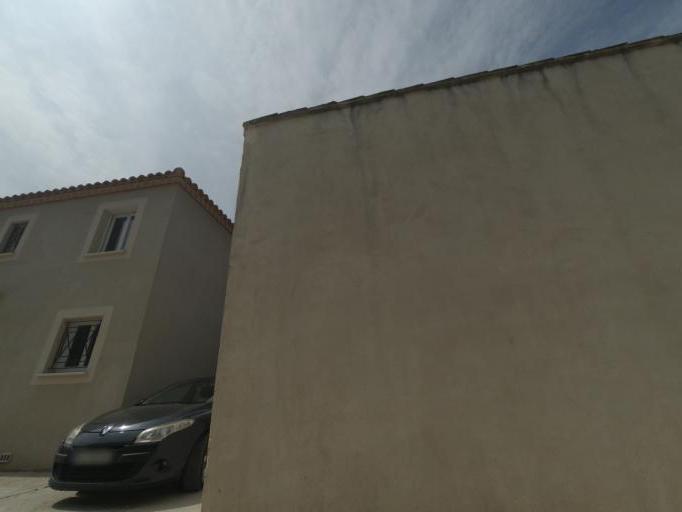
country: FR
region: Languedoc-Roussillon
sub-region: Departement du Gard
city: Congenies
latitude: 43.7767
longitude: 4.1590
